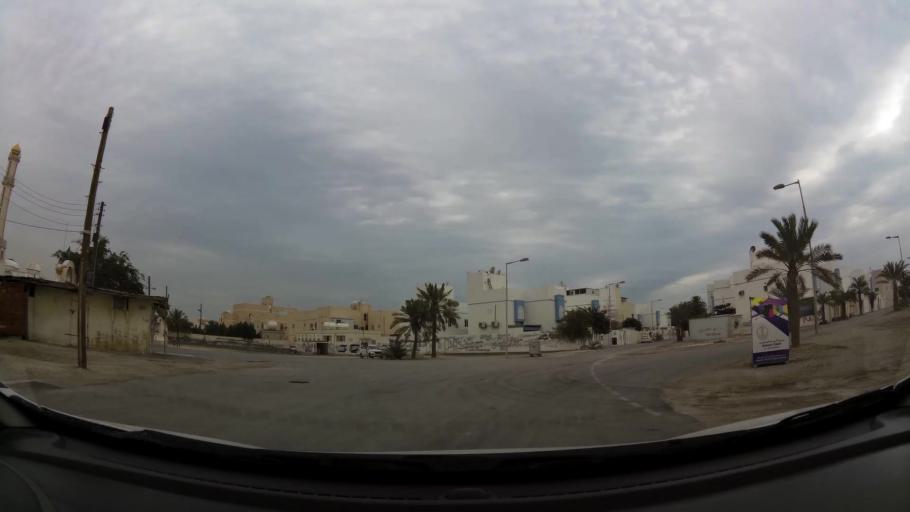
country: BH
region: Northern
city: Madinat `Isa
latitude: 26.1792
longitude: 50.5812
